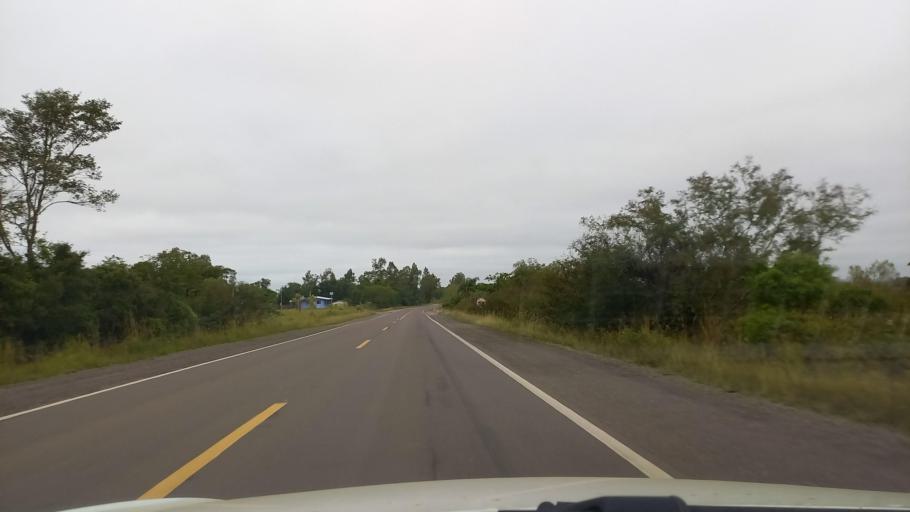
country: BR
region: Rio Grande do Sul
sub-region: Sao Pedro Do Sul
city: Sao Pedro do Sul
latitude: -29.7939
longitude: -54.1190
